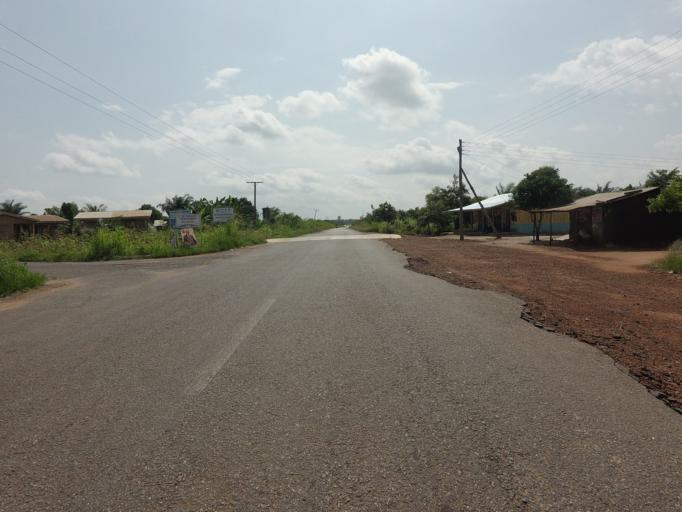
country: TG
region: Maritime
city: Lome
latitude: 6.2567
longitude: 0.9640
